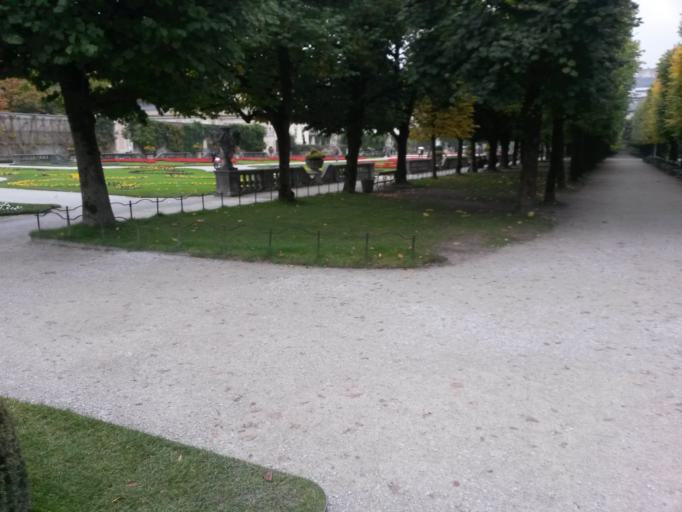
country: AT
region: Salzburg
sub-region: Salzburg Stadt
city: Salzburg
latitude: 47.8050
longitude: 13.0416
